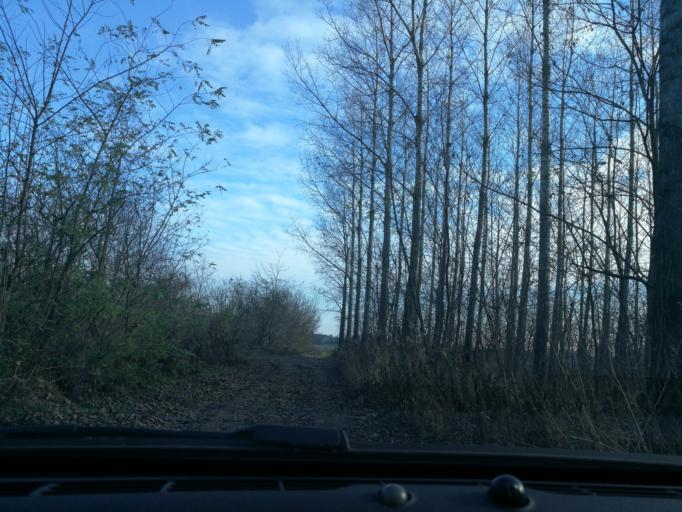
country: HU
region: Szabolcs-Szatmar-Bereg
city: Nyirpazony
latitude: 47.9593
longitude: 21.7698
